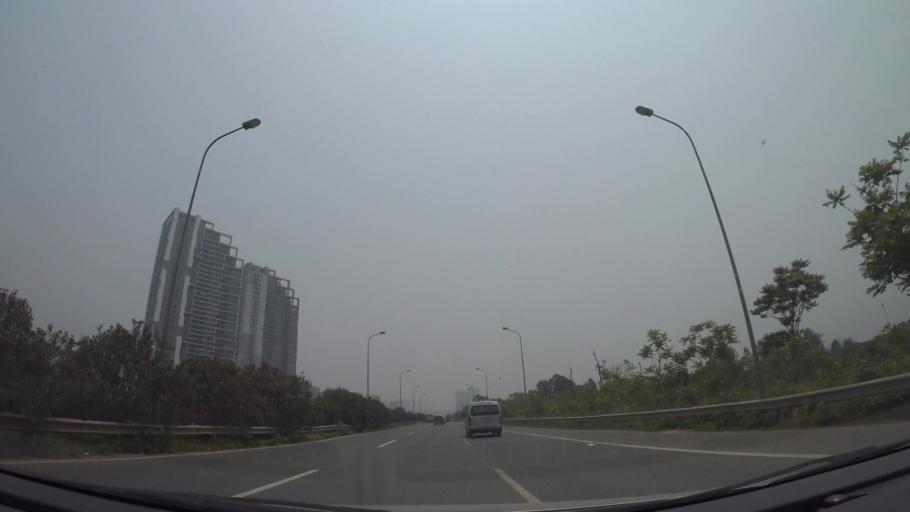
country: VN
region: Ha Noi
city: Cau Dien
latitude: 21.0053
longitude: 105.7668
